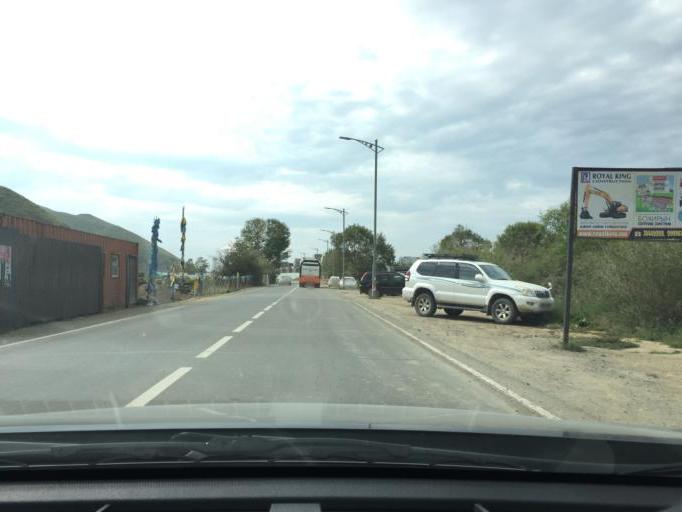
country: MN
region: Ulaanbaatar
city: Ulaanbaatar
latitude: 47.8845
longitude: 106.9512
